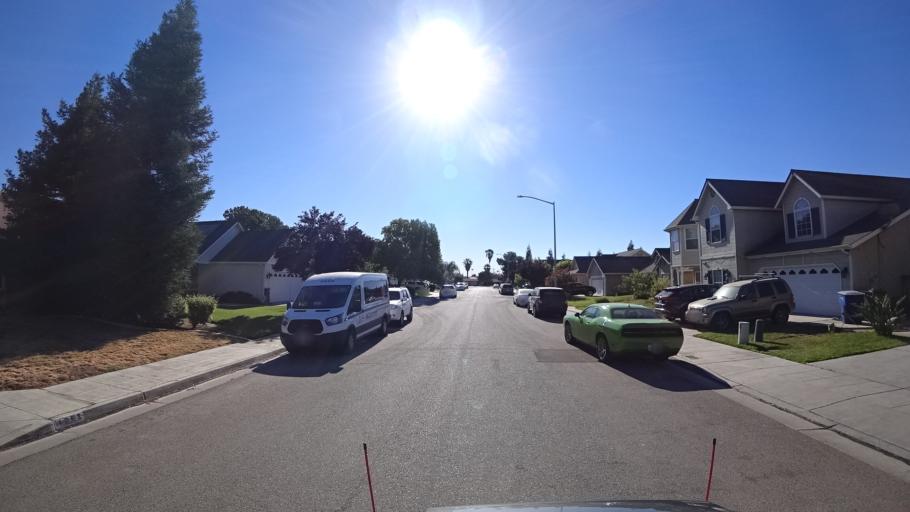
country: US
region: California
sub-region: Fresno County
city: West Park
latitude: 36.7824
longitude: -119.8639
